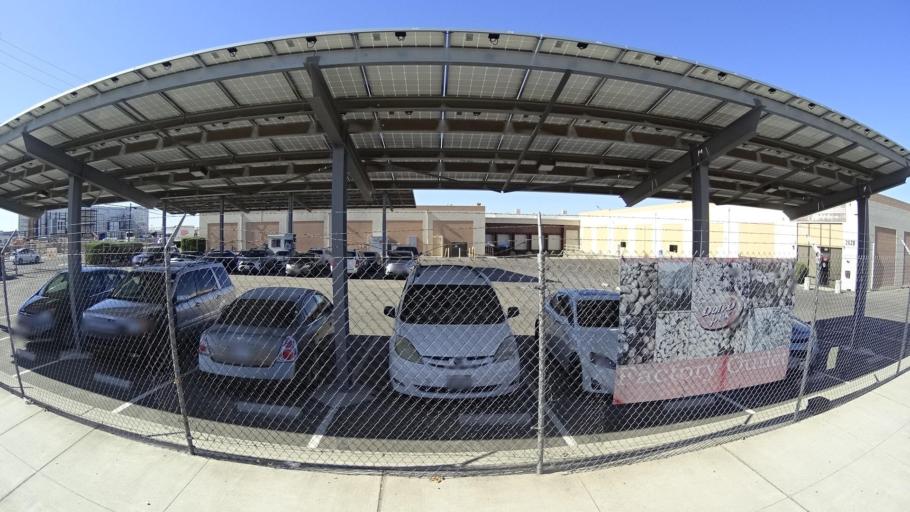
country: US
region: California
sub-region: Fresno County
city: Fresno
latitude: 36.7068
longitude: -119.7823
